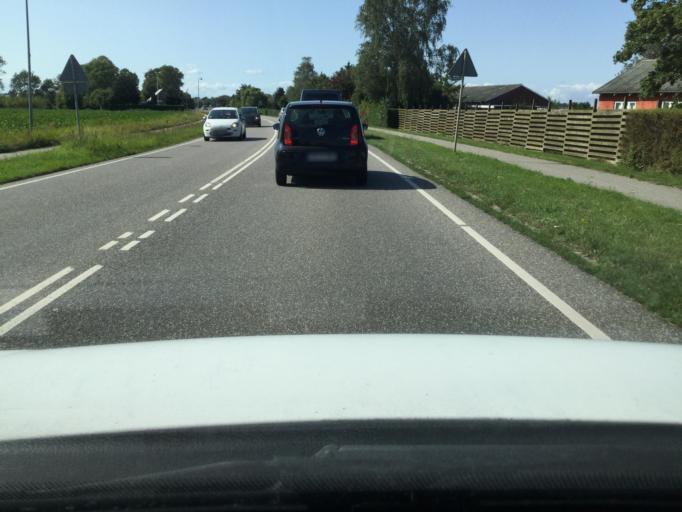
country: DK
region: Zealand
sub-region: Lolland Kommune
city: Nakskov
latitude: 54.8107
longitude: 11.2103
